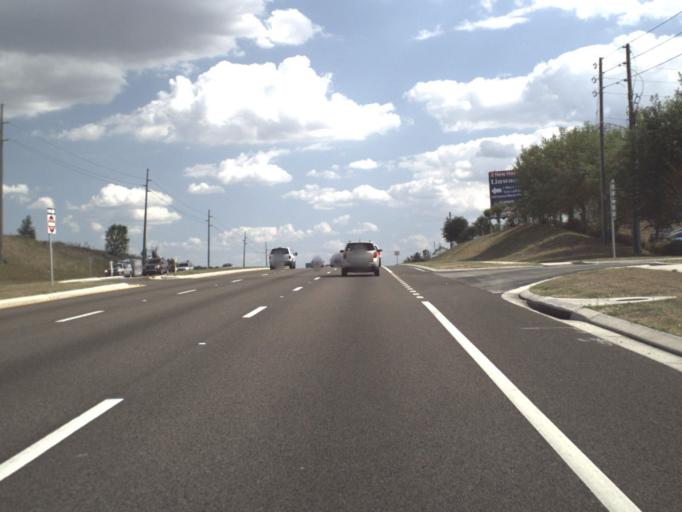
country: US
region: Florida
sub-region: Lake County
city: Clermont
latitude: 28.5319
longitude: -81.7349
